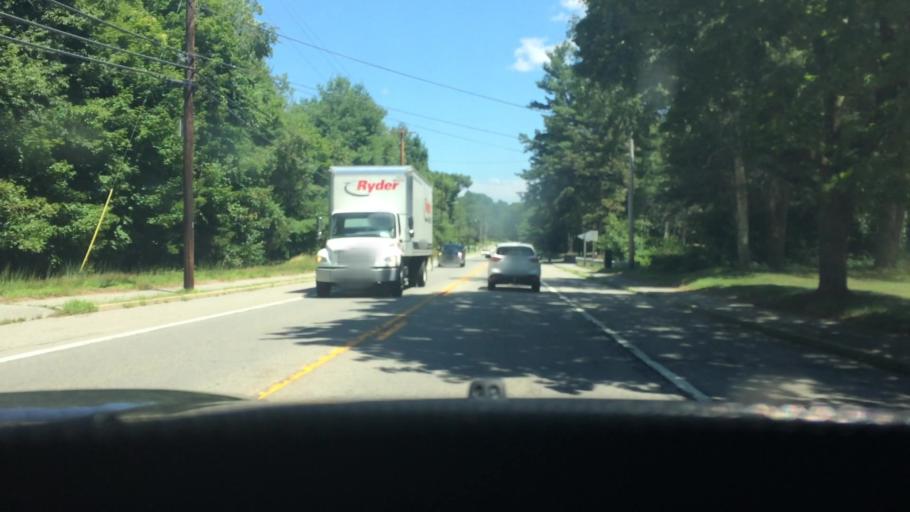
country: US
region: Massachusetts
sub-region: Worcester County
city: Millville
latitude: 42.0064
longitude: -71.5795
